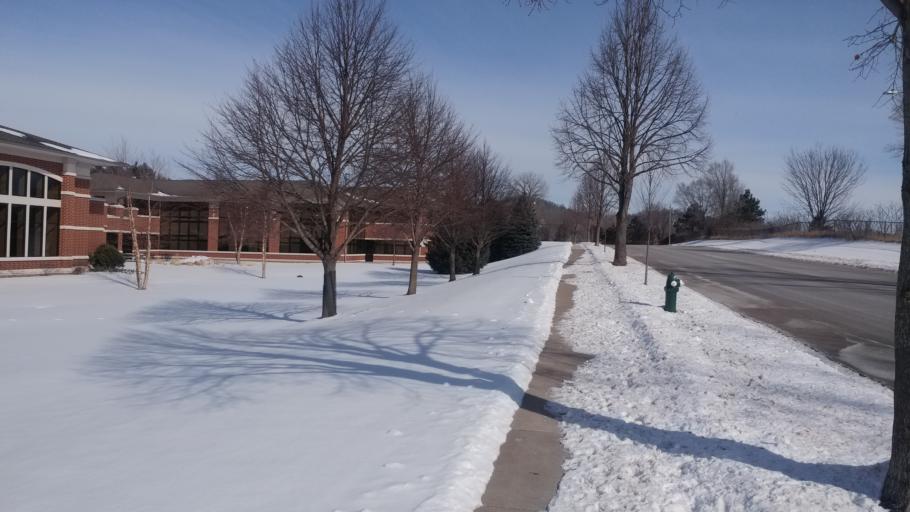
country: US
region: Wisconsin
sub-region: La Crosse County
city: Onalaska
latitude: 43.8758
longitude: -91.2121
